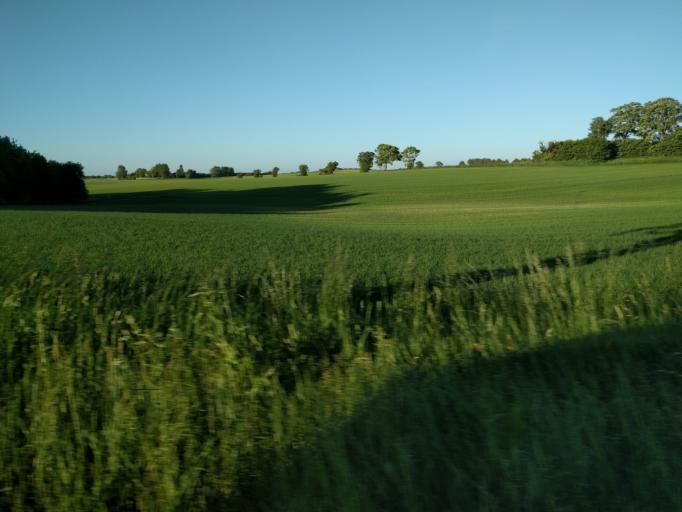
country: DK
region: South Denmark
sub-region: Kerteminde Kommune
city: Kerteminde
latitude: 55.5532
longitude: 10.6550
